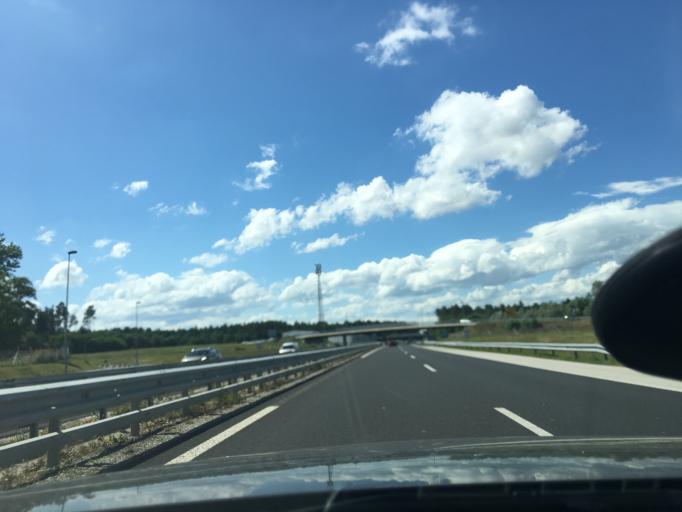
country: SI
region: Kidricevo
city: Kidricevo
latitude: 46.4106
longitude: 15.8130
